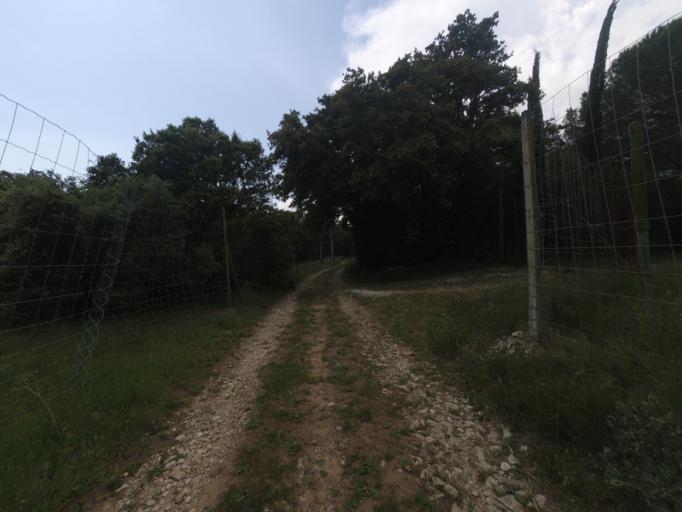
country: FR
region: Languedoc-Roussillon
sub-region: Departement du Gard
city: Vergeze
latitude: 43.7541
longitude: 4.2129
